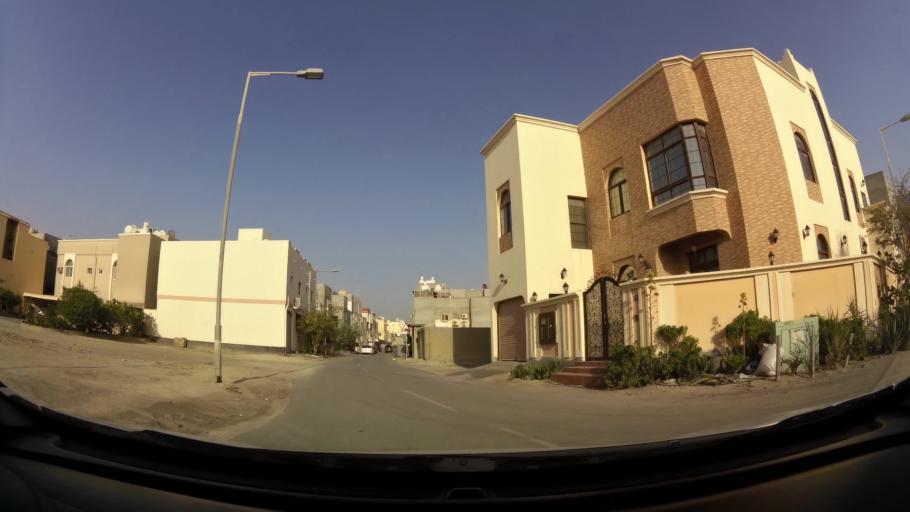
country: BH
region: Manama
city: Jidd Hafs
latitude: 26.2110
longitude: 50.5019
